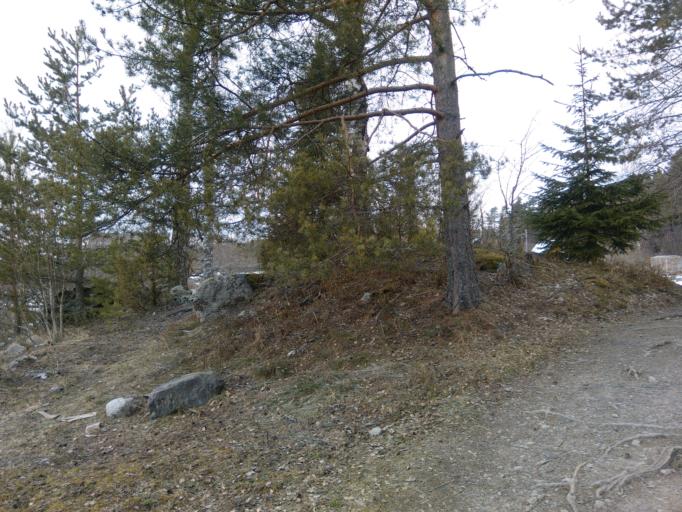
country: RU
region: Leningrad
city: Kuznechnoye
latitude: 61.0604
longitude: 29.9947
